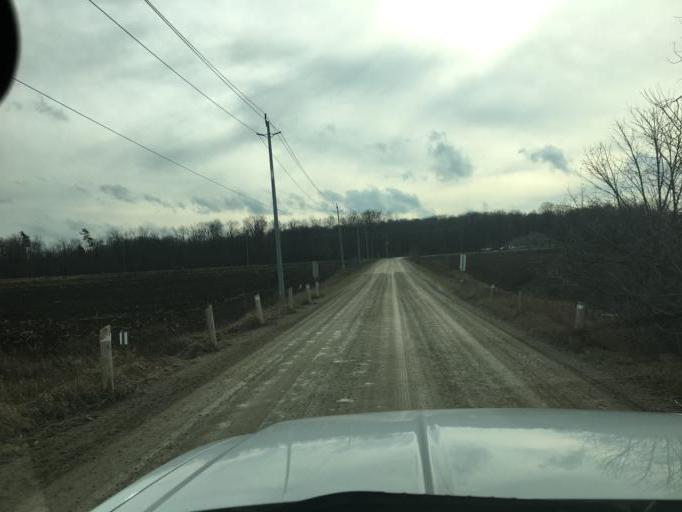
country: CA
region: Ontario
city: Waterloo
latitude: 43.4998
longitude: -80.5825
